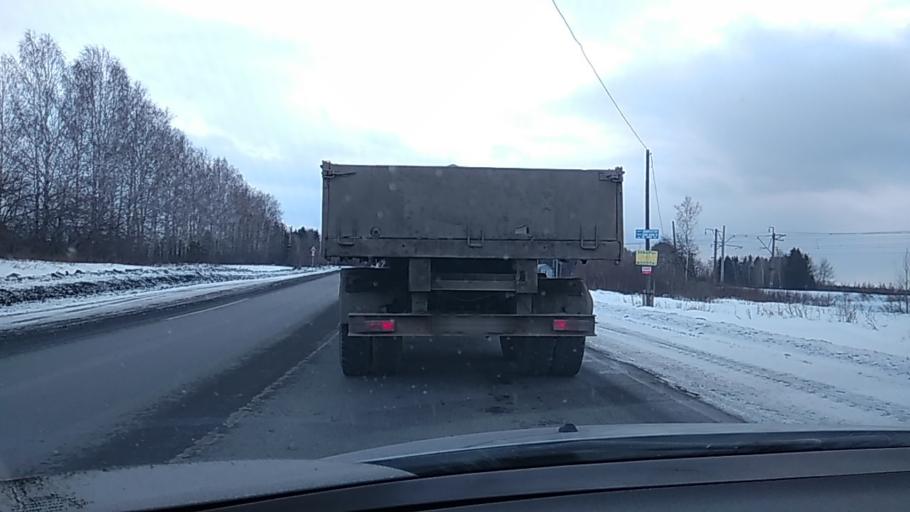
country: RU
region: Sverdlovsk
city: Sovkhoznyy
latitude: 56.6046
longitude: 61.3018
